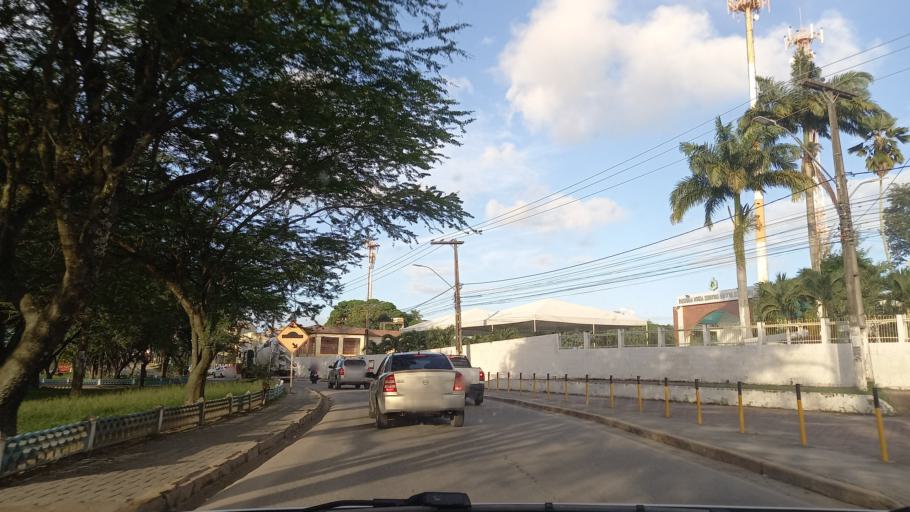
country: BR
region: Pernambuco
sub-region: Jaboatao Dos Guararapes
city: Jaboatao
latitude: -8.2387
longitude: -34.9842
